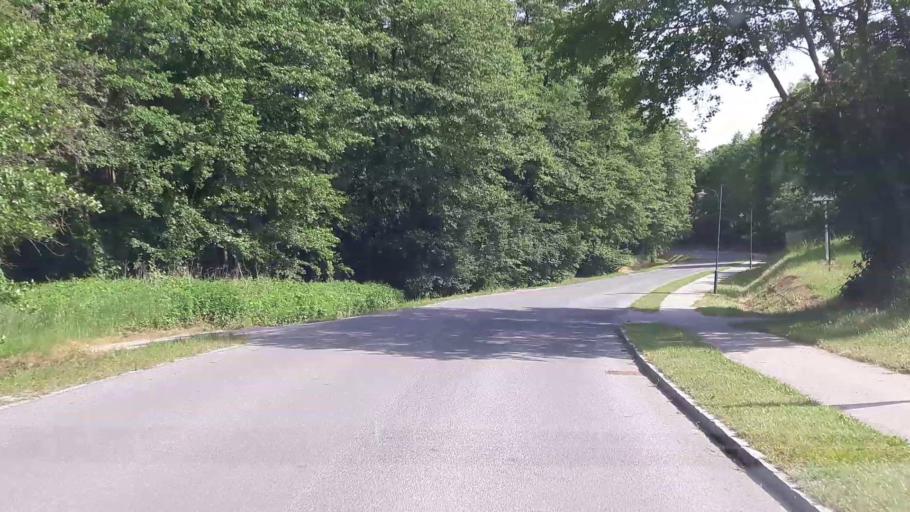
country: AT
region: Burgenland
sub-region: Politischer Bezirk Gussing
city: Stegersbach
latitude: 47.1675
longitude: 16.1486
